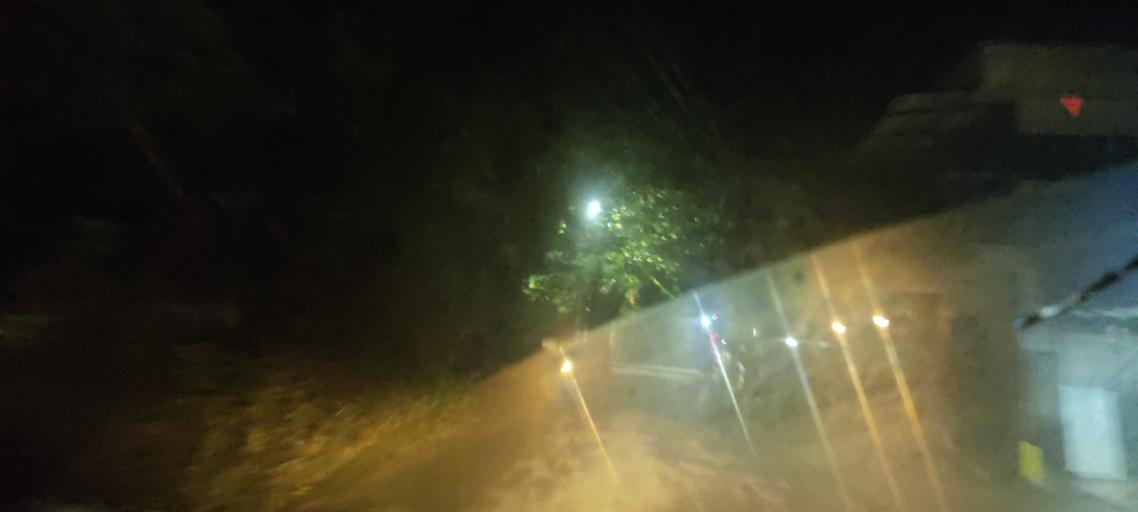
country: IN
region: Kerala
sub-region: Alappuzha
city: Vayalar
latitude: 9.7229
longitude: 76.3370
